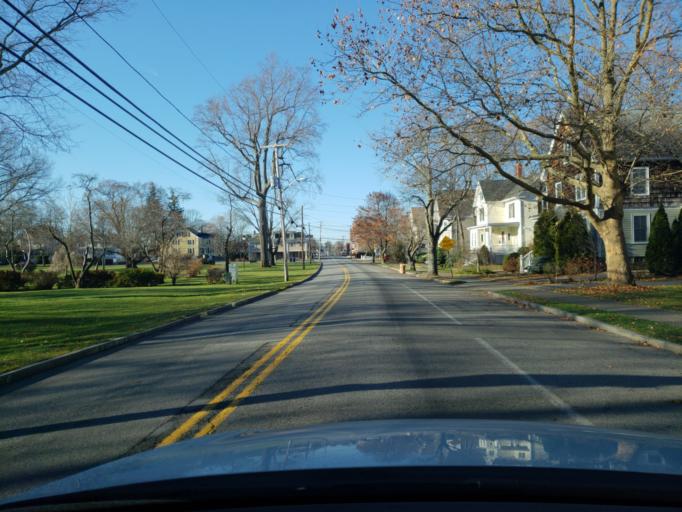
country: US
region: Massachusetts
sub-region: Essex County
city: Andover
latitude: 42.6563
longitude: -71.1364
